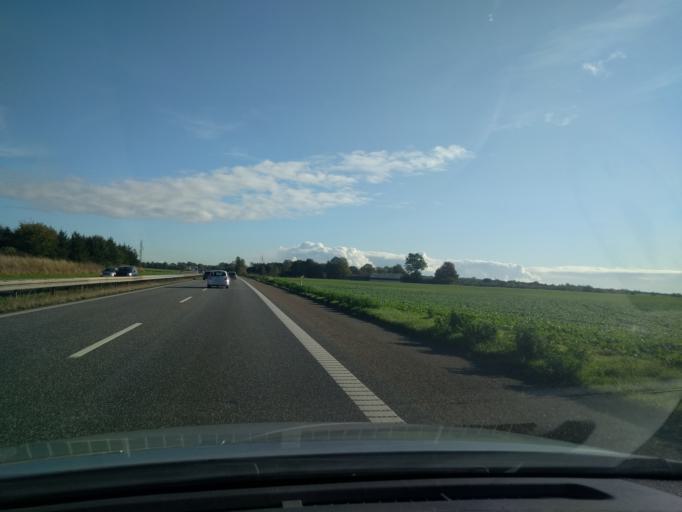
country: DK
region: Zealand
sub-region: Ringsted Kommune
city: Ringsted
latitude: 55.4497
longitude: 11.6859
